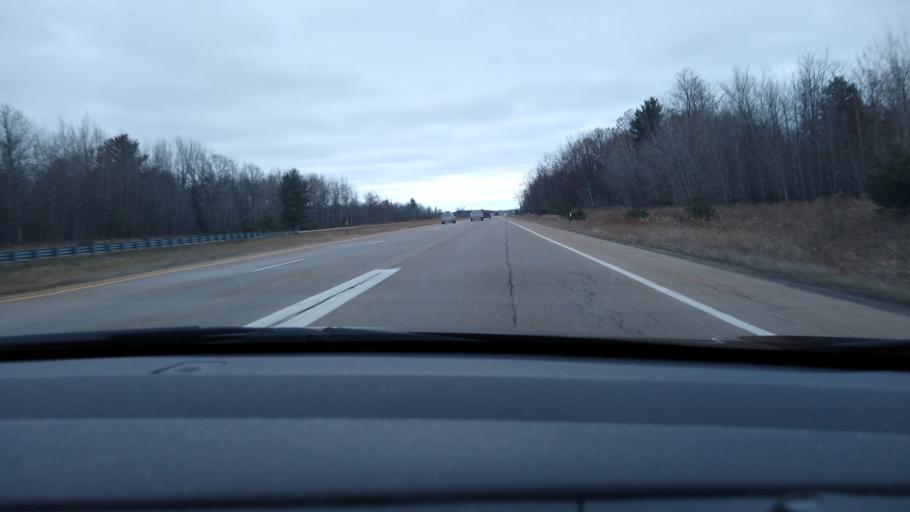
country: US
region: Michigan
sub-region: Roscommon County
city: Houghton Lake
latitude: 44.3402
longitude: -84.8072
